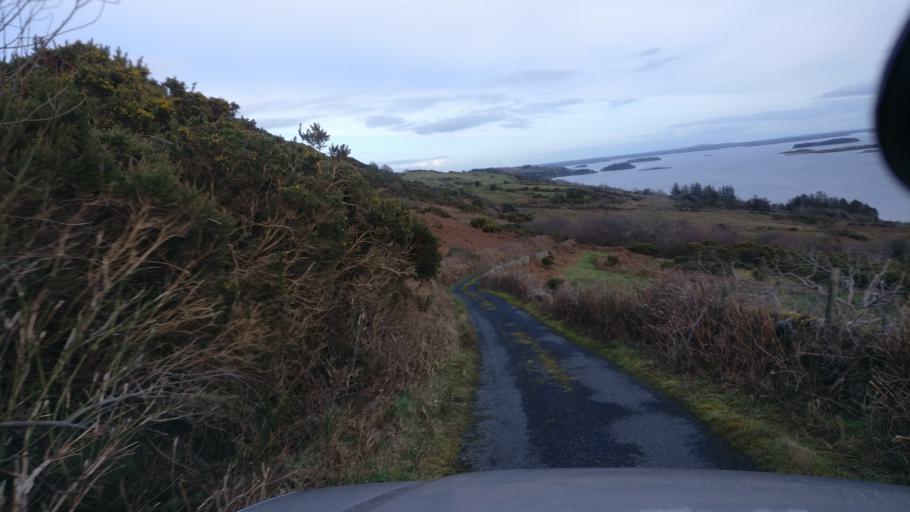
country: IE
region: Connaught
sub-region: County Galway
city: Oughterard
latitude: 53.5213
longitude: -9.4035
